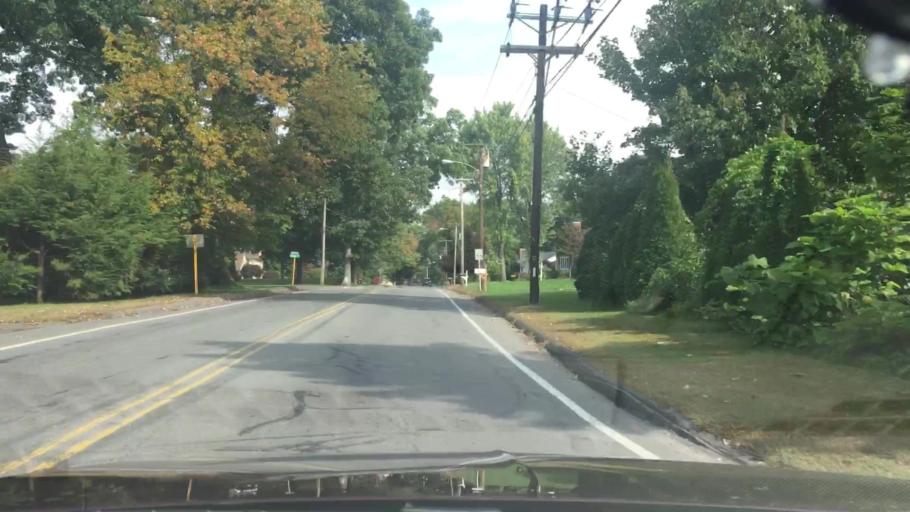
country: US
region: Massachusetts
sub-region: Hampden County
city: East Longmeadow
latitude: 42.0596
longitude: -72.5303
